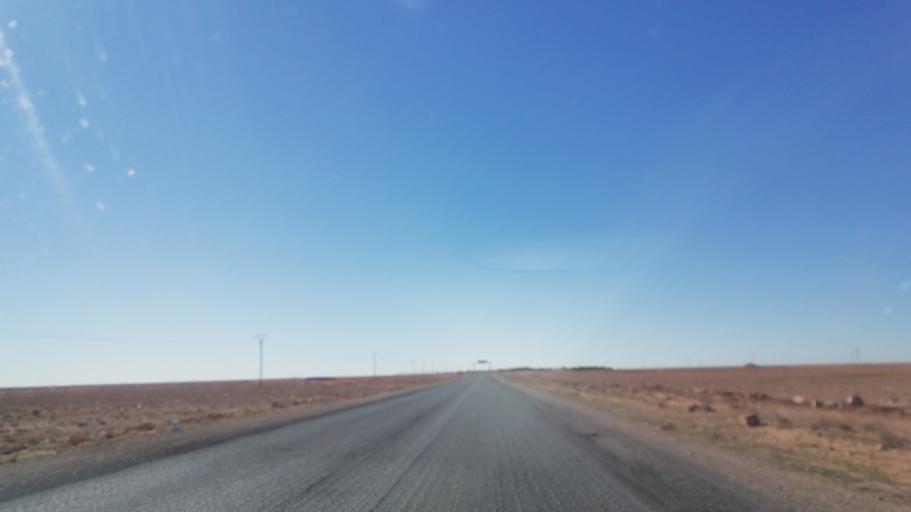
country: DZ
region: Saida
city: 'Ain el Hadjar
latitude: 34.0100
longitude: 0.0528
